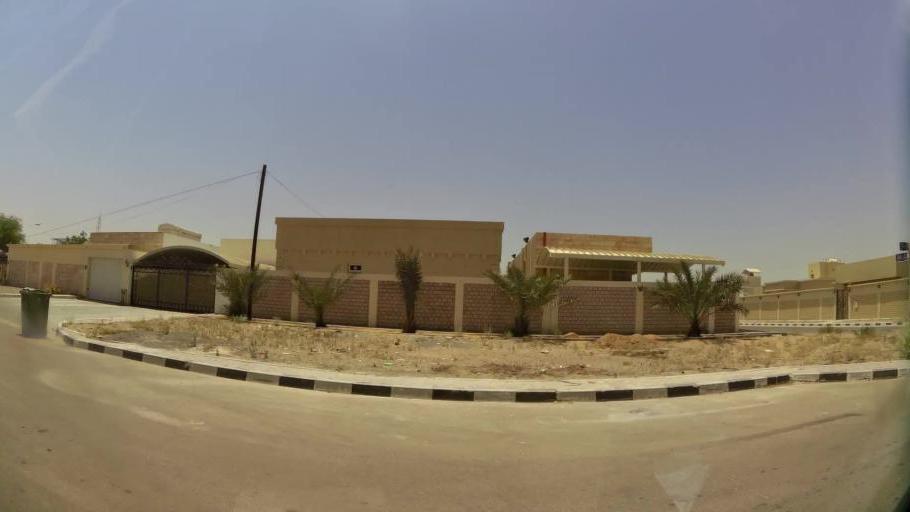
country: AE
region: Ajman
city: Ajman
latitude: 25.4192
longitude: 55.5032
